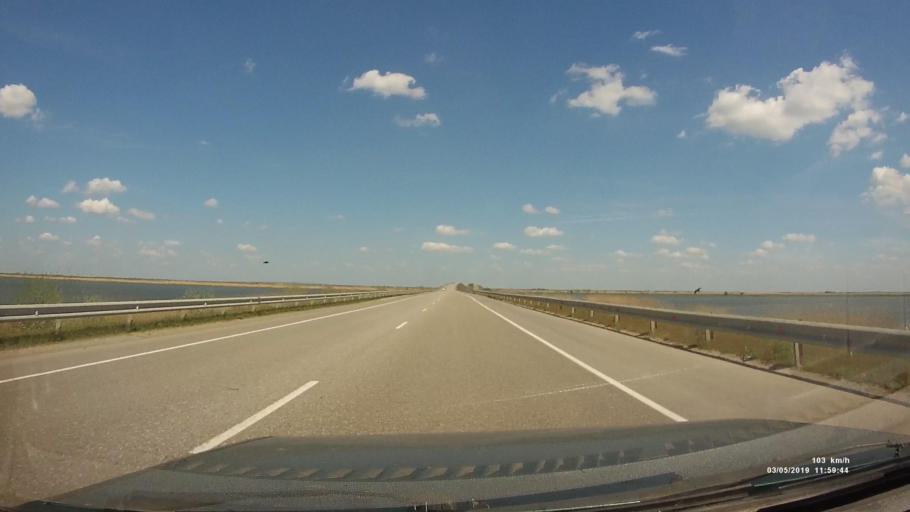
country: RU
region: Rostov
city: Bagayevskaya
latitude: 47.2387
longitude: 40.3331
